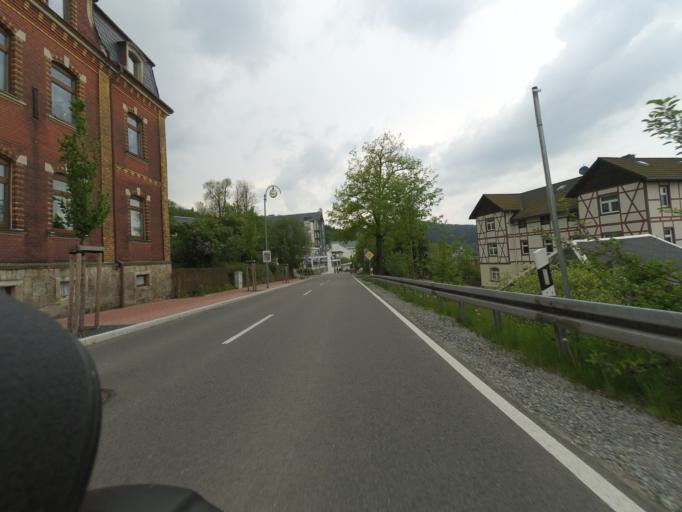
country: DE
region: Saxony
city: Thermalbad Wiesenbad
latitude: 50.6180
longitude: 13.0467
